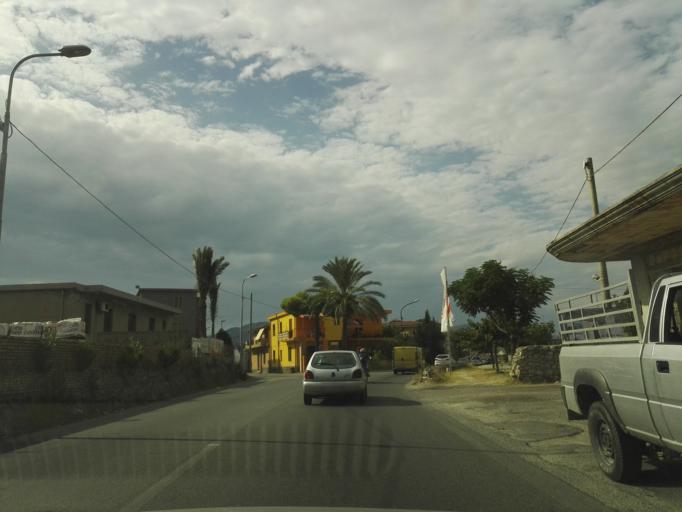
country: IT
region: Calabria
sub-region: Provincia di Catanzaro
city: Marina di Davoli
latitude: 38.6603
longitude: 16.5452
